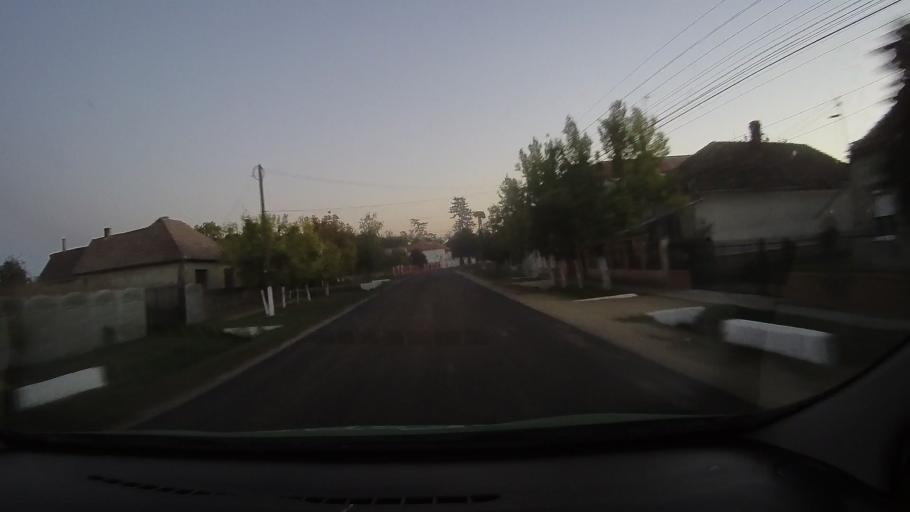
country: RO
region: Bihor
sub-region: Comuna Simian
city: Simian
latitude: 47.4993
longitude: 22.0911
